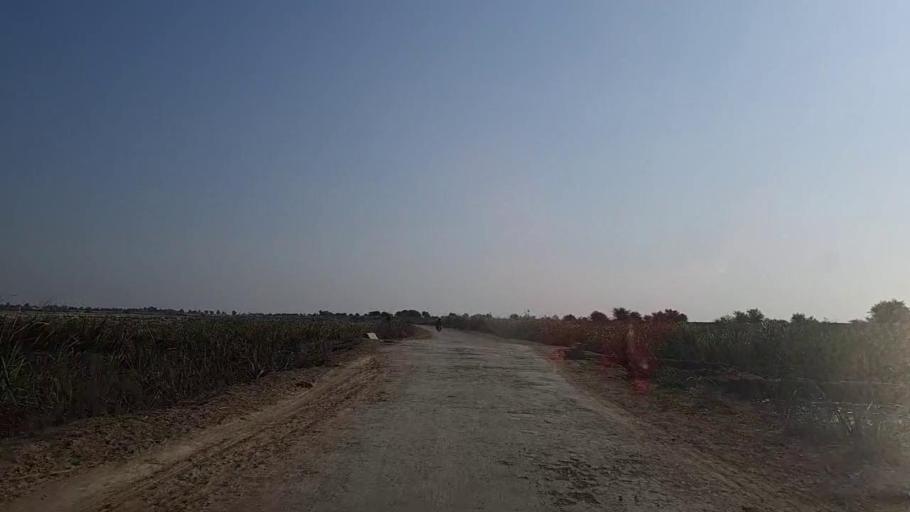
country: PK
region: Sindh
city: Sanghar
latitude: 25.9824
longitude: 69.0233
